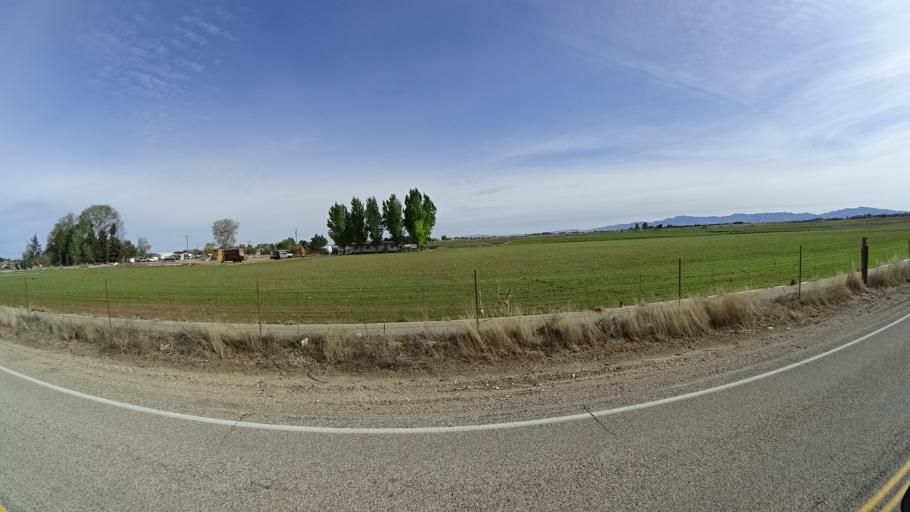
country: US
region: Idaho
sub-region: Ada County
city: Kuna
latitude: 43.4735
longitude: -116.3532
